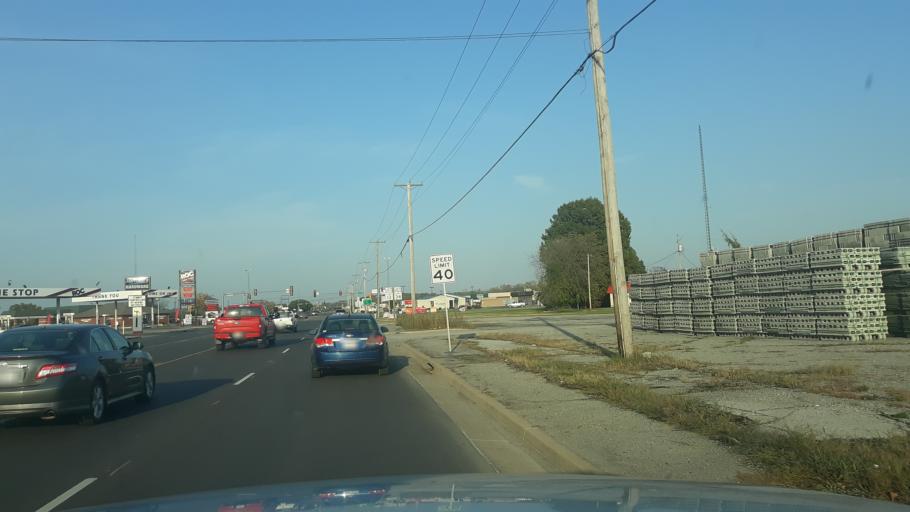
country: US
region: Illinois
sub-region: Saline County
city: Harrisburg
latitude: 37.7404
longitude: -88.5309
